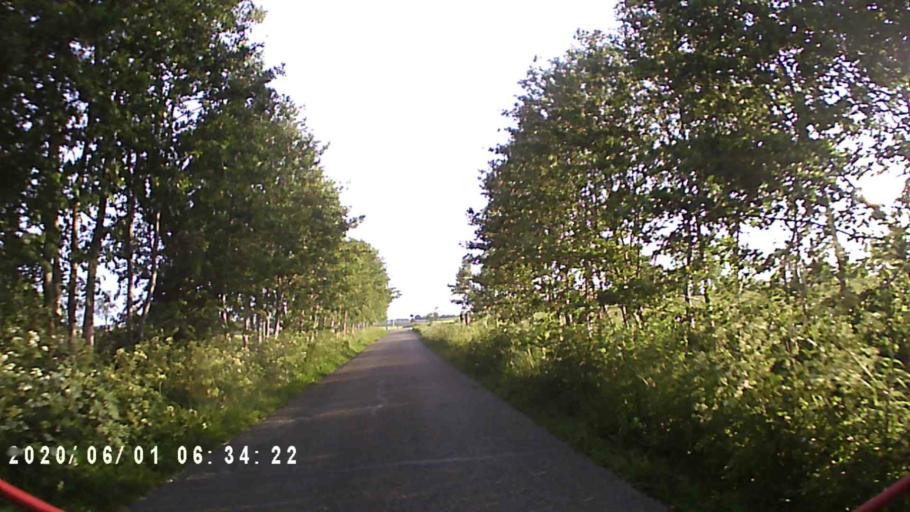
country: NL
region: Friesland
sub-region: Gemeente Kollumerland en Nieuwkruisland
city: Kollum
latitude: 53.2792
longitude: 6.1663
